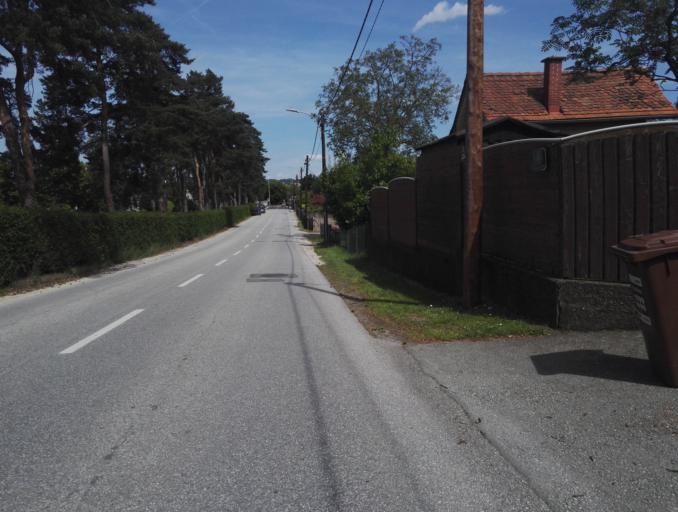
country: AT
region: Styria
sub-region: Graz Stadt
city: Wetzelsdorf
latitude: 47.0430
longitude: 15.4262
